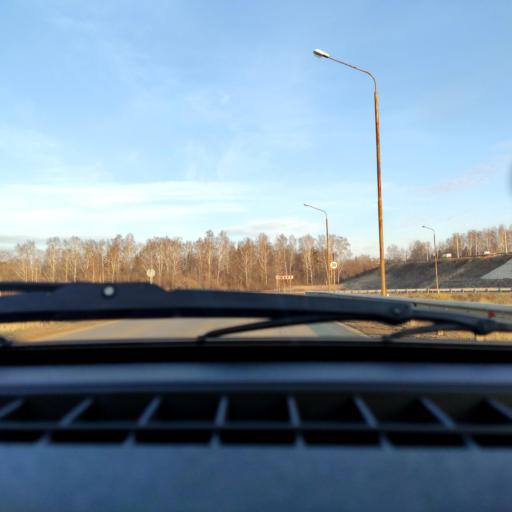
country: RU
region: Bashkortostan
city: Iglino
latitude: 54.7712
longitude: 56.2576
